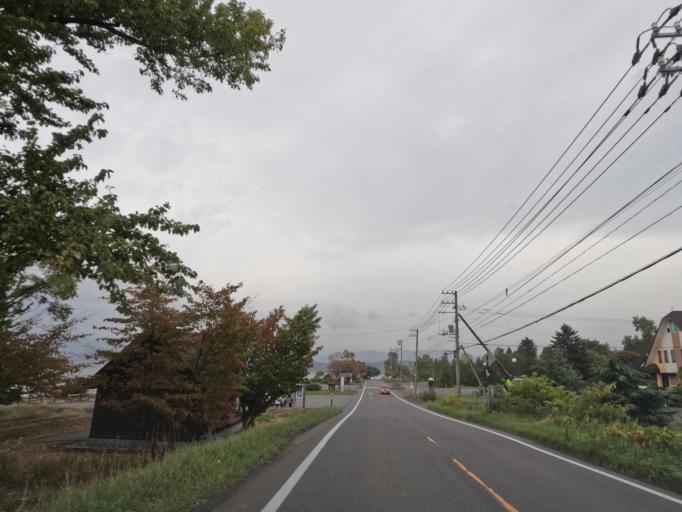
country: JP
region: Hokkaido
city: Date
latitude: 42.5640
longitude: 140.8417
